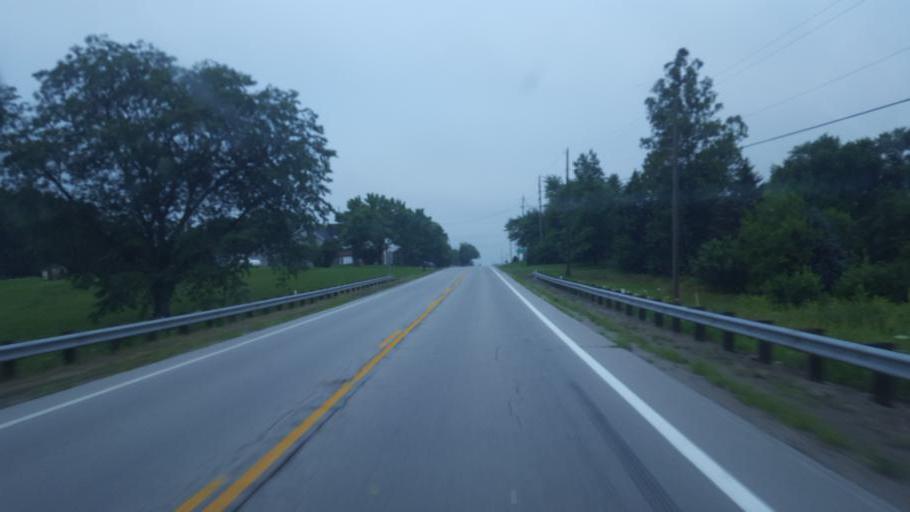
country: US
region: Ohio
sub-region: Madison County
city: Mount Sterling
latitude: 39.6504
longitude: -83.3305
